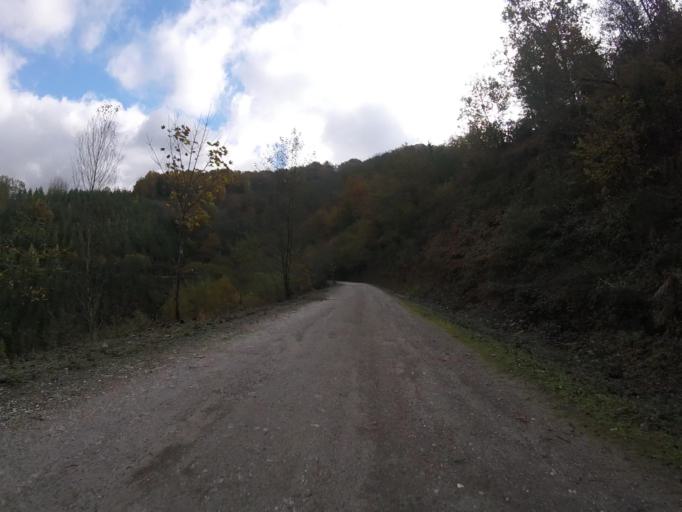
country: ES
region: Navarre
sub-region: Provincia de Navarra
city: Goizueta
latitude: 43.2206
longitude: -1.8453
